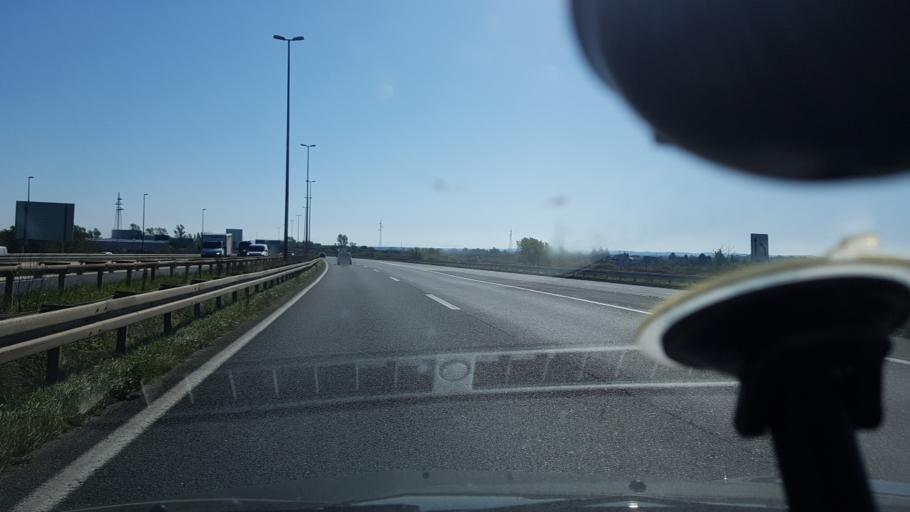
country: HR
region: Grad Zagreb
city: Zadvorsko
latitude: 45.7559
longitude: 15.9030
